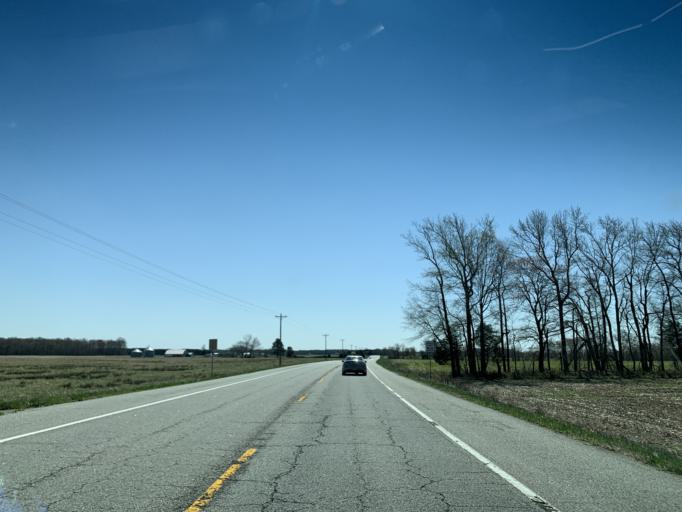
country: US
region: Maryland
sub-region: Queen Anne's County
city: Centreville
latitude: 38.9649
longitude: -75.9950
